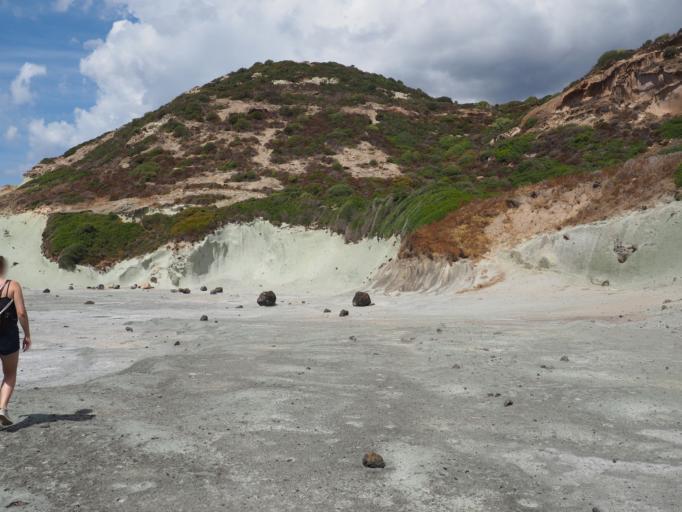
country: IT
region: Sardinia
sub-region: Provincia di Oristano
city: Bosa
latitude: 40.2937
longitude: 8.4731
